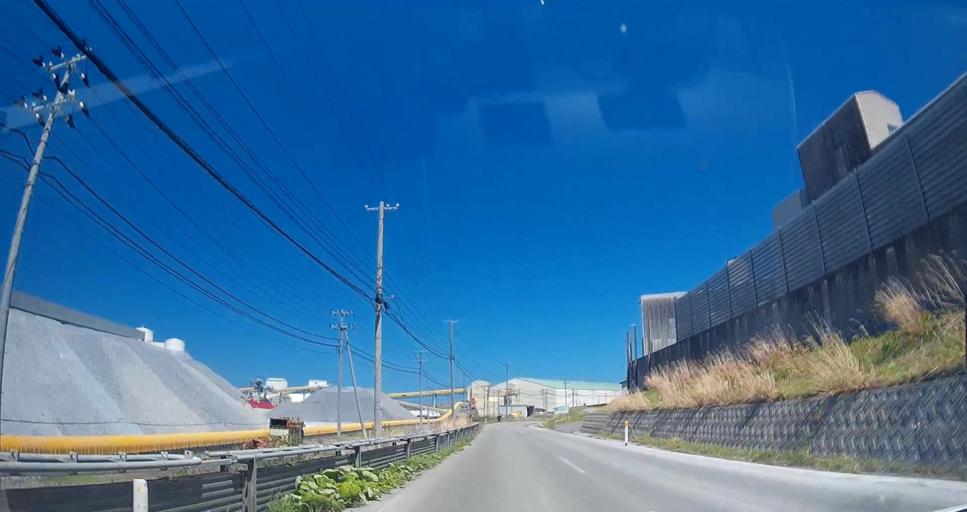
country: JP
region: Aomori
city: Mutsu
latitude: 41.4097
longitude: 141.4392
